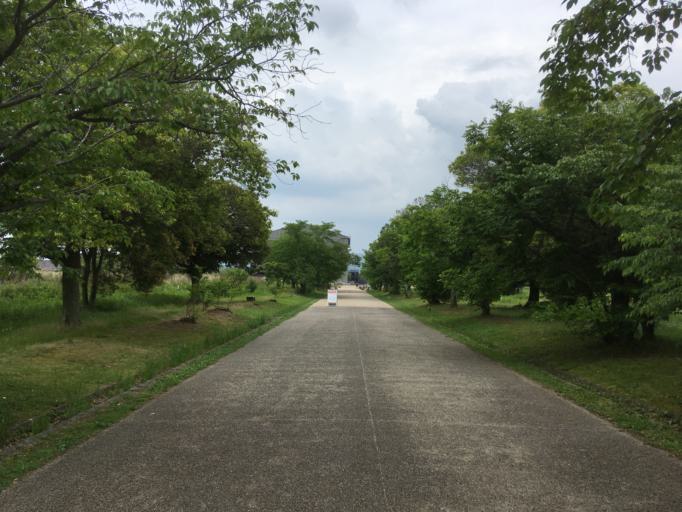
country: JP
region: Nara
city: Nara-shi
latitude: 34.6915
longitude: 135.7909
